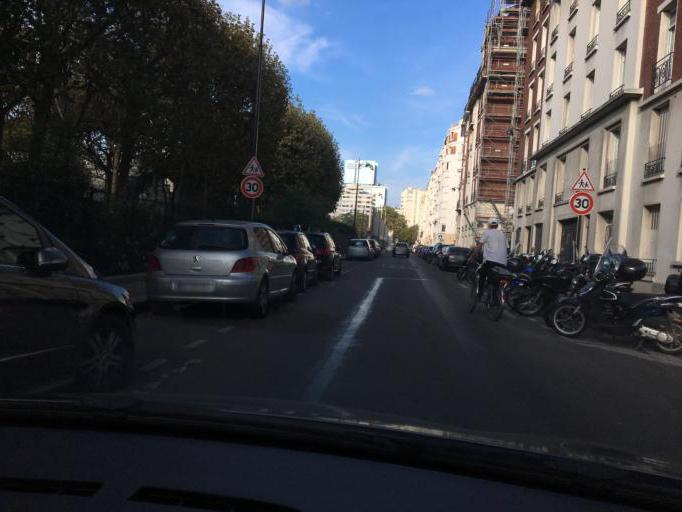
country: FR
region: Ile-de-France
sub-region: Departement des Hauts-de-Seine
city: Levallois-Perret
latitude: 48.8894
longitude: 2.2989
